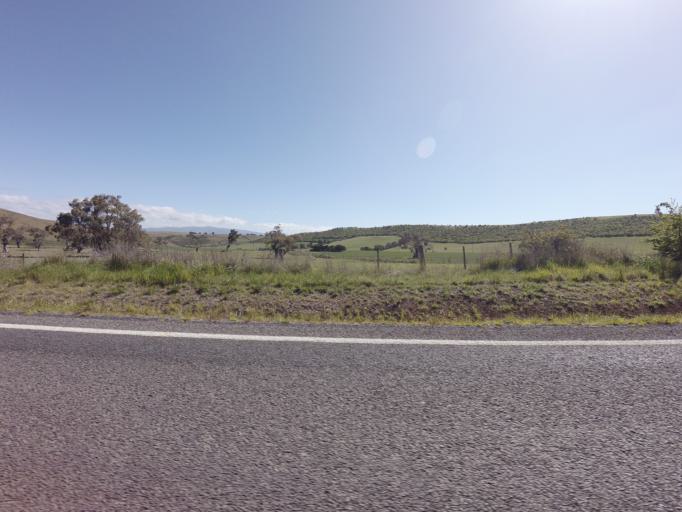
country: AU
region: Tasmania
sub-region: Derwent Valley
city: New Norfolk
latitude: -42.5689
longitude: 146.8808
